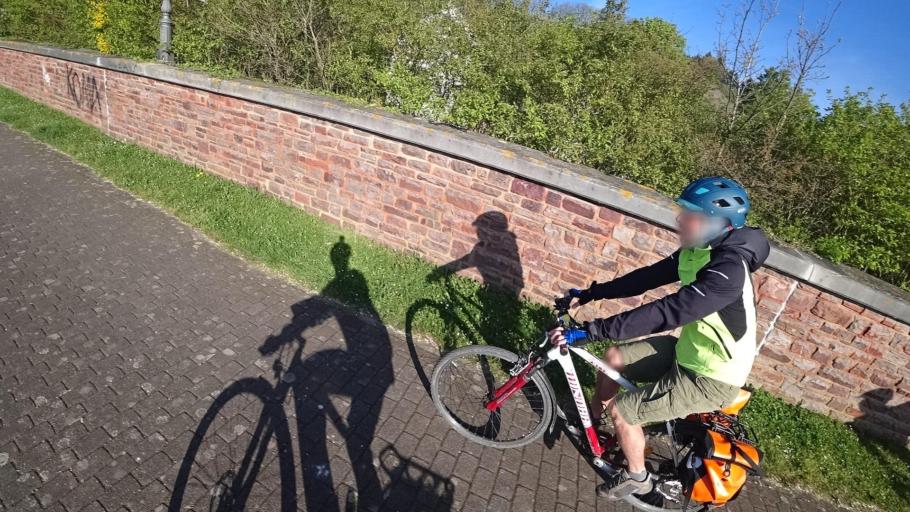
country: DE
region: Rheinland-Pfalz
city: Saarburg
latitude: 49.6101
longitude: 6.5584
